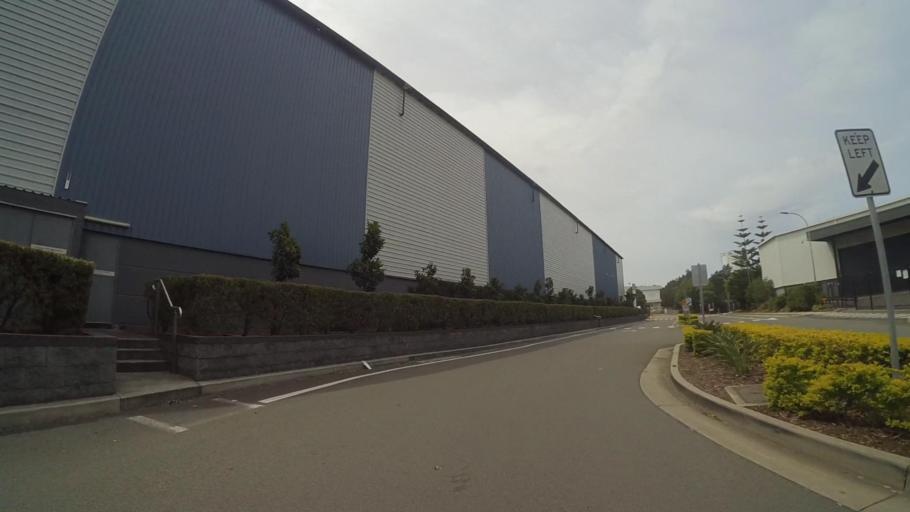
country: AU
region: New South Wales
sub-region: Botany Bay
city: Mascot
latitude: -33.9237
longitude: 151.1773
